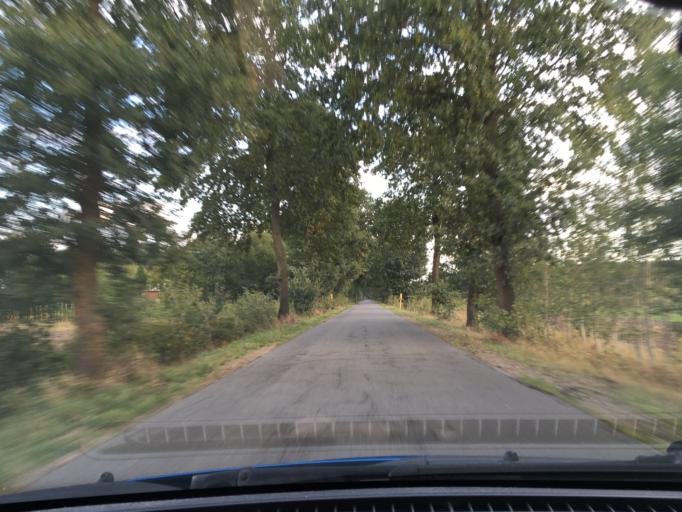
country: DE
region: Lower Saxony
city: Vierhofen
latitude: 53.2772
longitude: 10.2021
